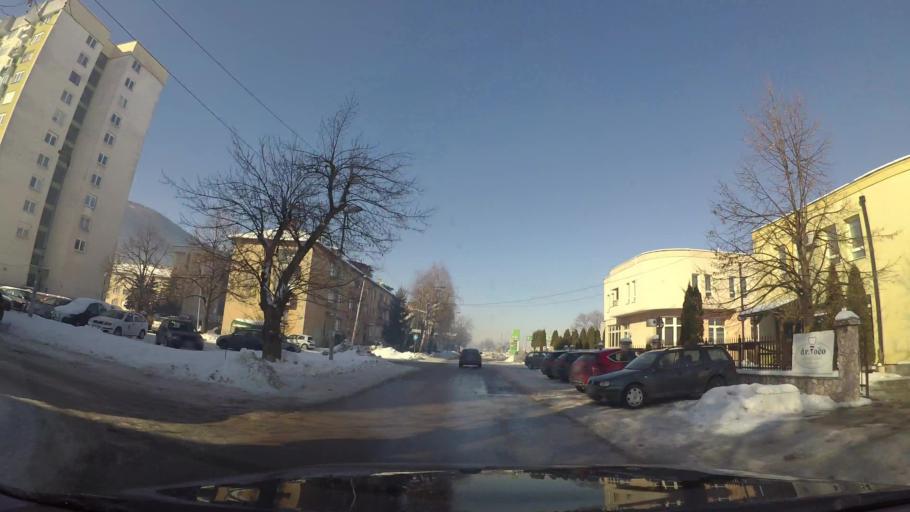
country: BA
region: Federation of Bosnia and Herzegovina
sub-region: Kanton Sarajevo
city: Sarajevo
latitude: 43.7993
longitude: 18.3125
